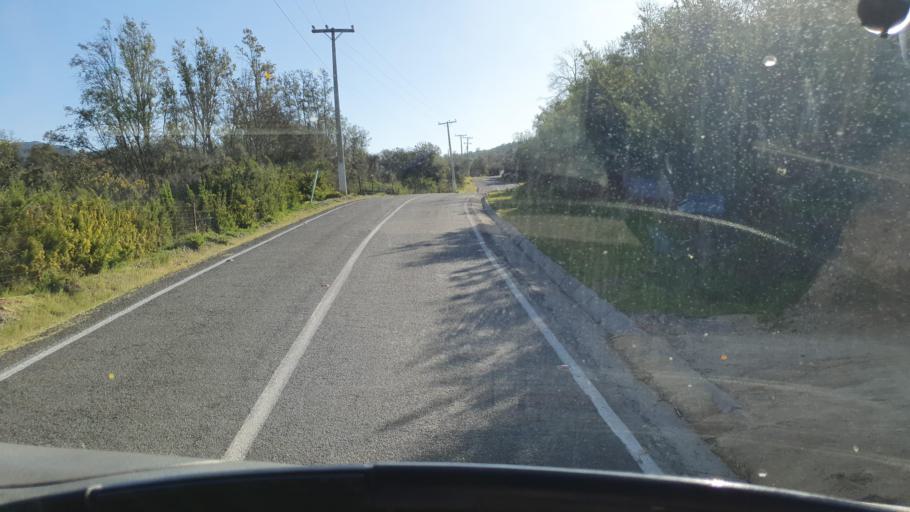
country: CL
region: Valparaiso
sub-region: Provincia de Marga Marga
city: Limache
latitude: -33.1943
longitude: -71.2091
